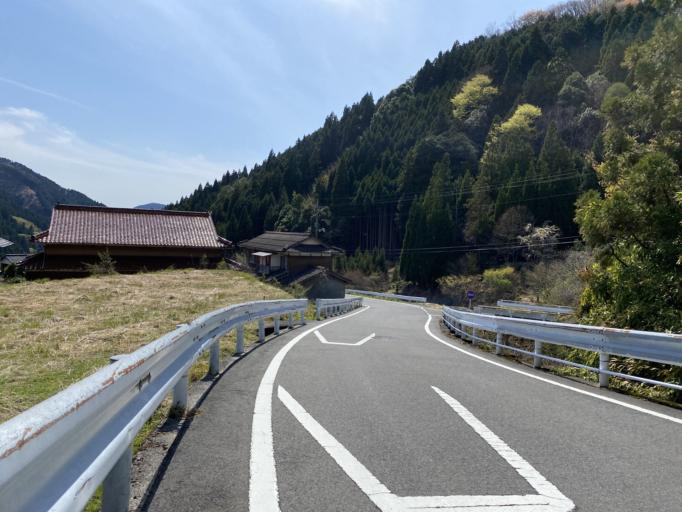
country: JP
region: Hyogo
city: Yamazakicho-nakabirose
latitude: 35.1751
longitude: 134.3527
